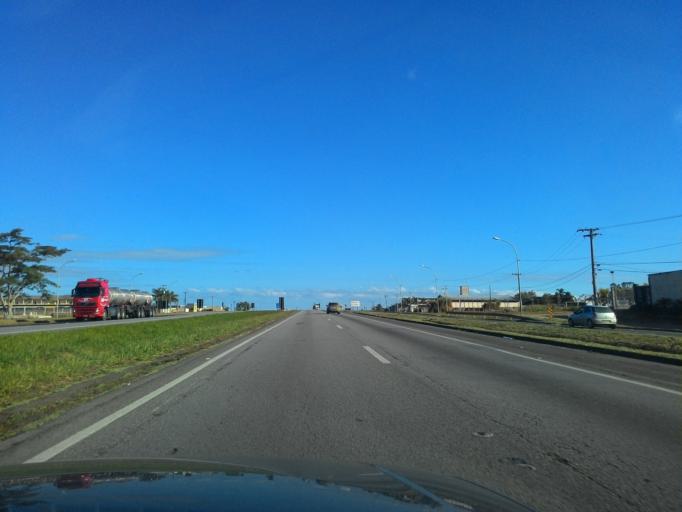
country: BR
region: Sao Paulo
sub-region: Registro
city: Registro
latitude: -24.5115
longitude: -47.8504
